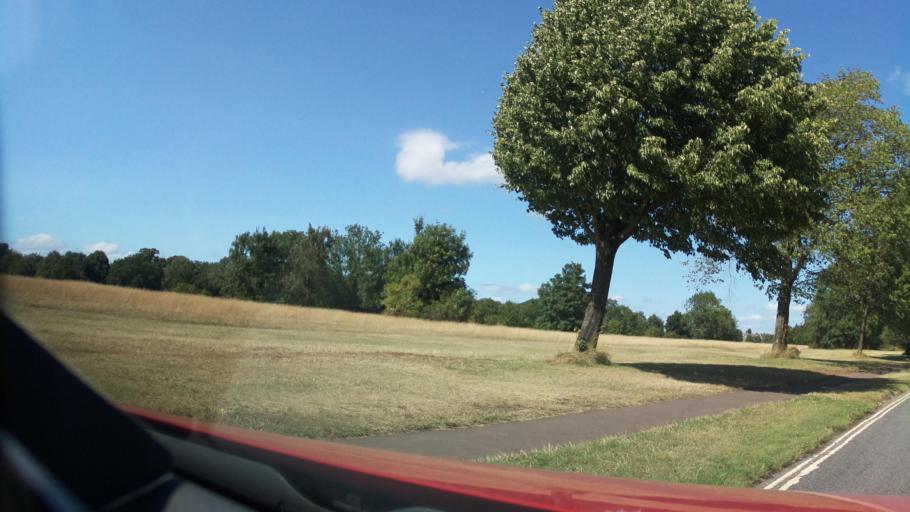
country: GB
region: England
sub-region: Bristol
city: Bristol
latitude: 51.4652
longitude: -2.6268
